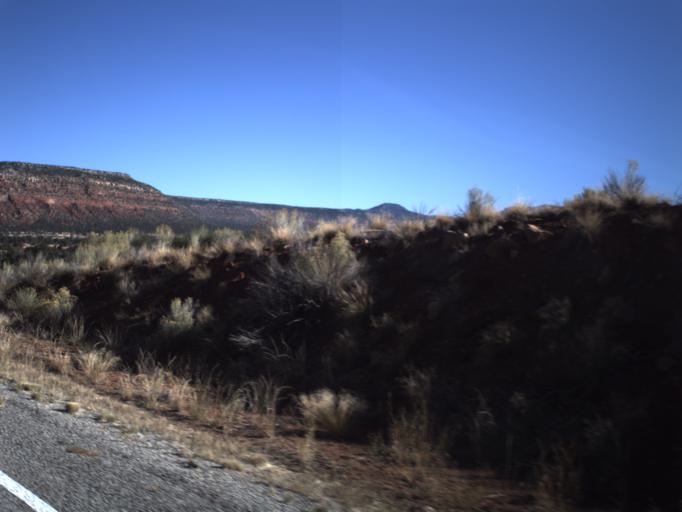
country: US
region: Utah
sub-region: San Juan County
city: Blanding
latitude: 37.5865
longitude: -110.0400
